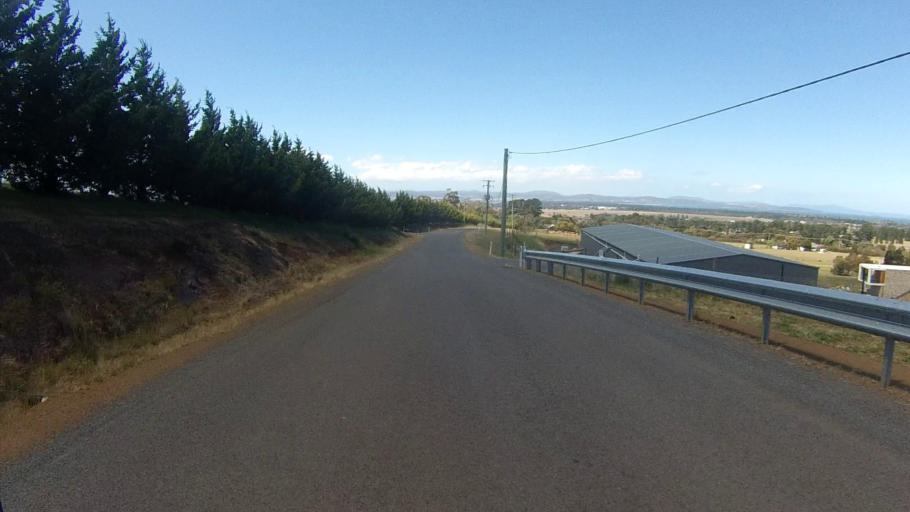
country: AU
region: Tasmania
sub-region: Clarence
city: Cambridge
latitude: -42.8423
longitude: 147.4541
